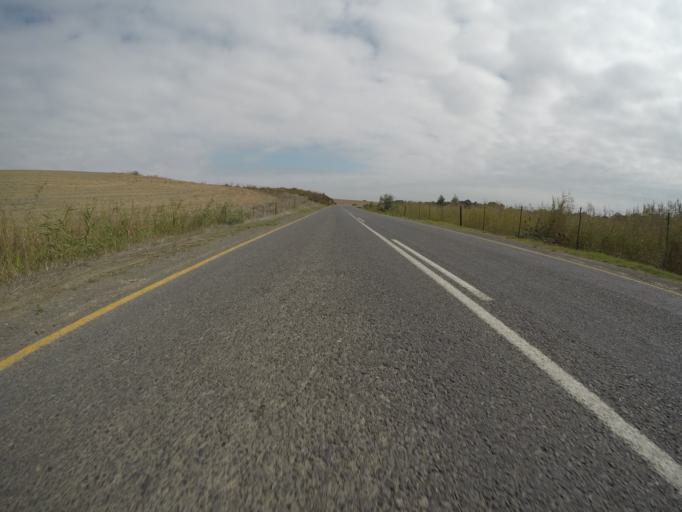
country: ZA
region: Western Cape
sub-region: City of Cape Town
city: Sunset Beach
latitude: -33.7895
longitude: 18.5527
